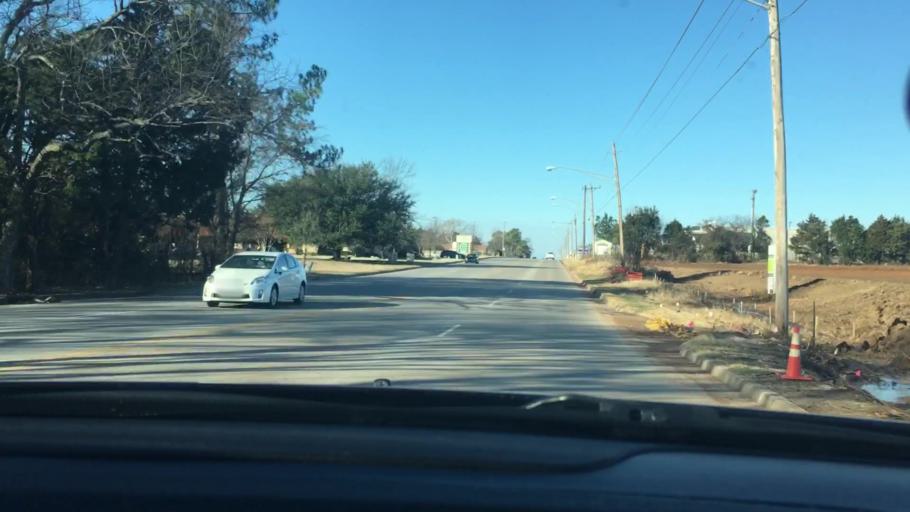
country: US
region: Oklahoma
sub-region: Carter County
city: Ardmore
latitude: 34.1876
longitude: -97.1500
